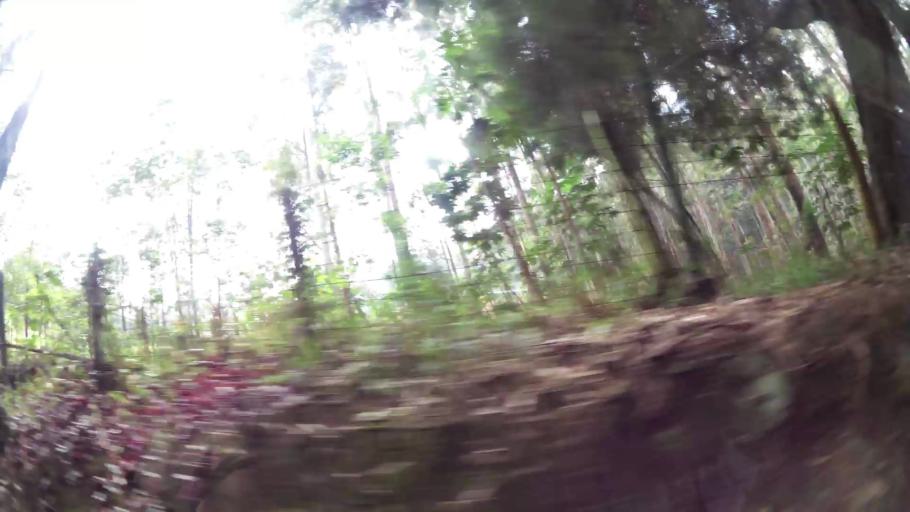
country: CO
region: Antioquia
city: Medellin
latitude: 6.2044
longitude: -75.5482
